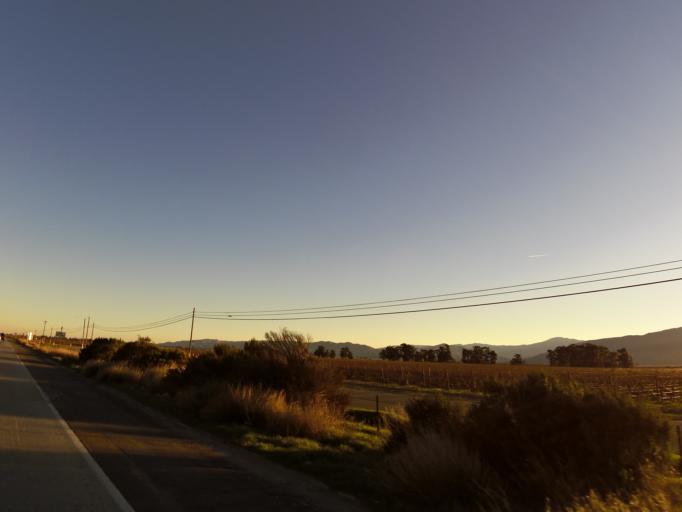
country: US
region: California
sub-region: Monterey County
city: Soledad
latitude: 36.3821
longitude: -121.2994
